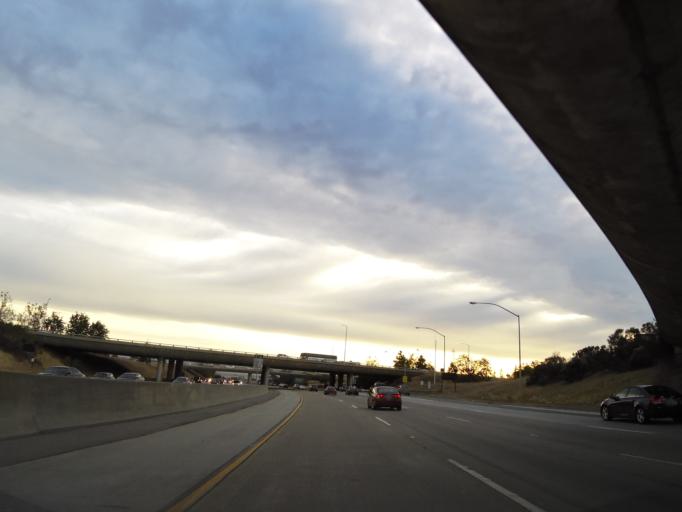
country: US
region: California
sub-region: Santa Clara County
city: Cupertino
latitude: 37.3321
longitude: -122.0576
